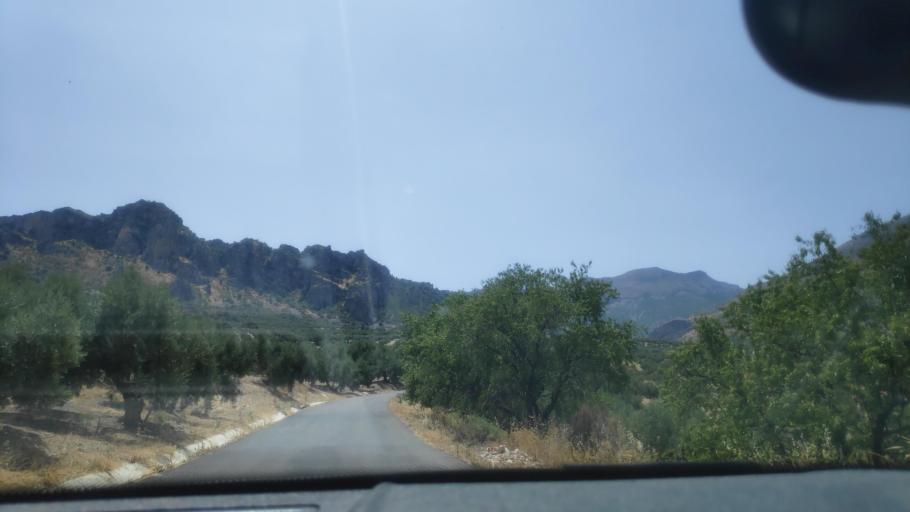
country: ES
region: Andalusia
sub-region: Provincia de Jaen
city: Jimena
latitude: 37.7972
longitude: -3.4483
